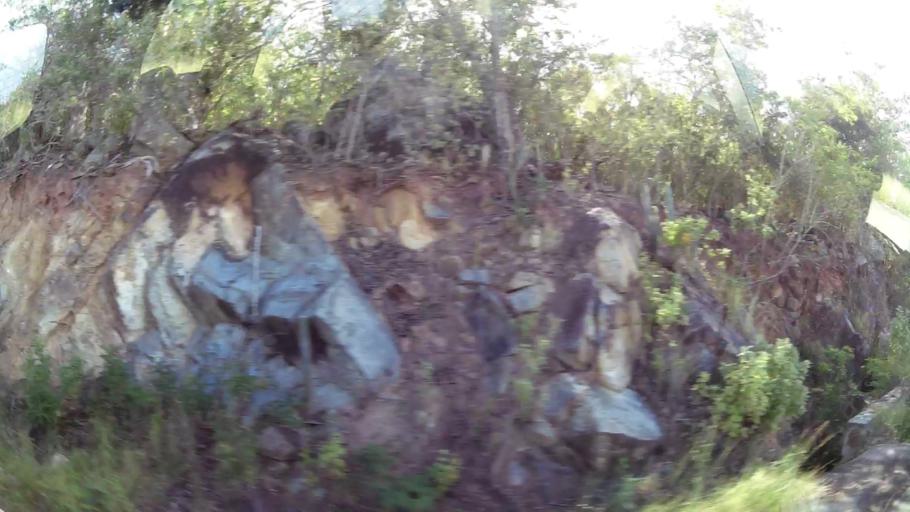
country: VG
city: Tortola
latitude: 18.5000
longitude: -64.4077
